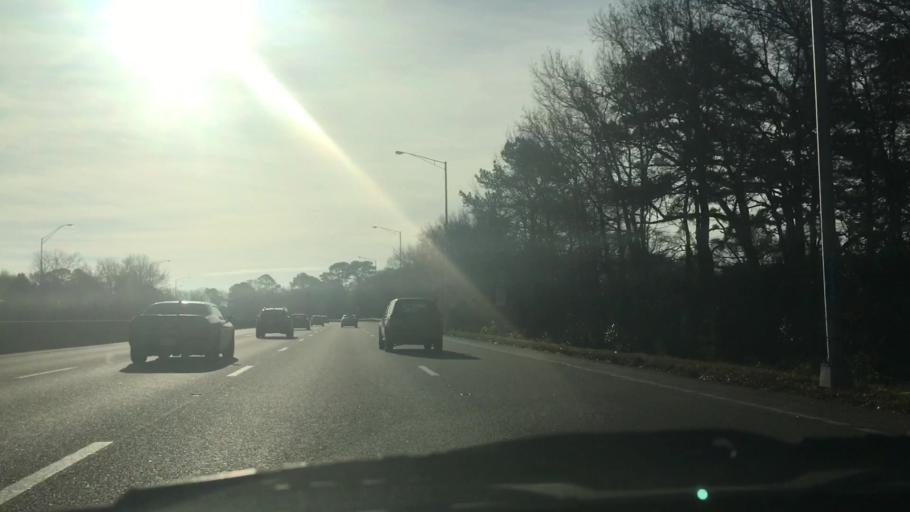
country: US
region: Virginia
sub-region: City of Norfolk
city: Norfolk
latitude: 36.8891
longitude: -76.2298
